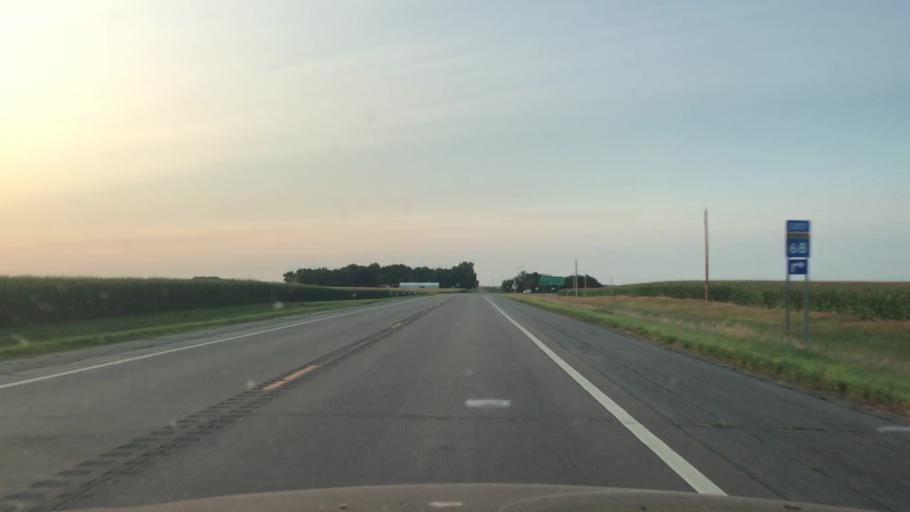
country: US
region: Minnesota
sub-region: Redwood County
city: Redwood Falls
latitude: 44.4096
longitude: -95.1276
